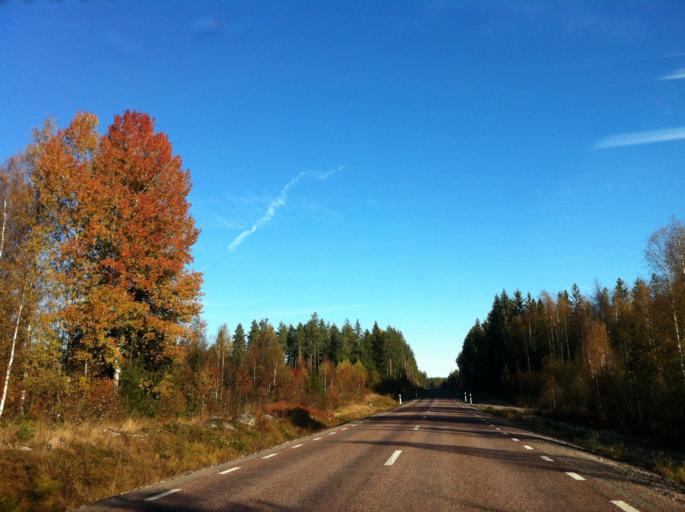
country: SE
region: Gaevleborg
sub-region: Gavle Kommun
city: Gavle
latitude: 60.5767
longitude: 17.1288
